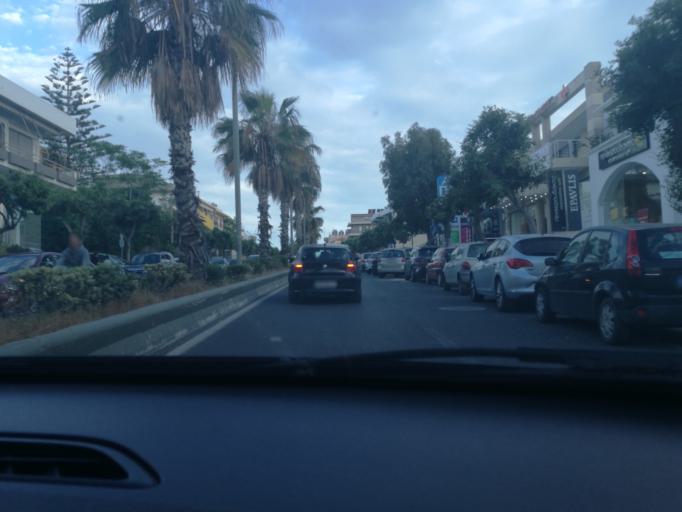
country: GR
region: Crete
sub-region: Nomos Irakleiou
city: Irakleion
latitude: 35.3189
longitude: 25.1446
